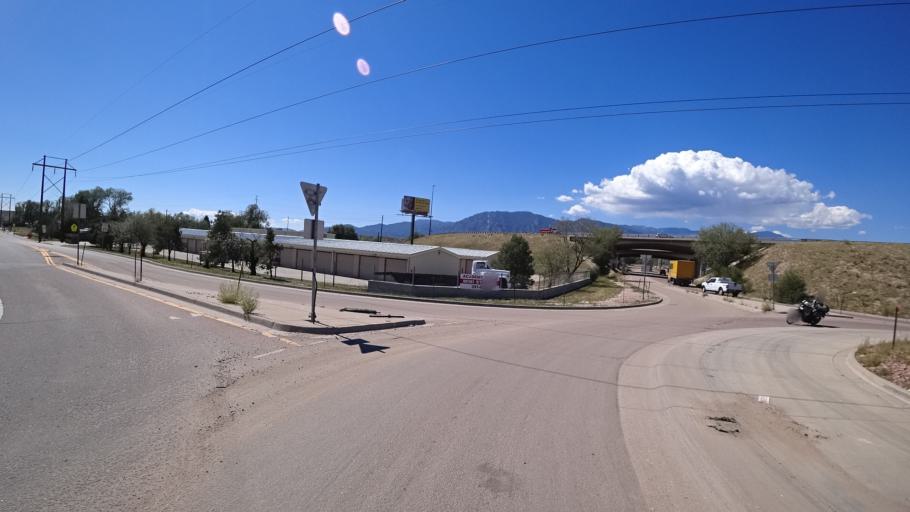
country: US
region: Colorado
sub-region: El Paso County
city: Stratmoor
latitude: 38.7699
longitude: -104.7571
